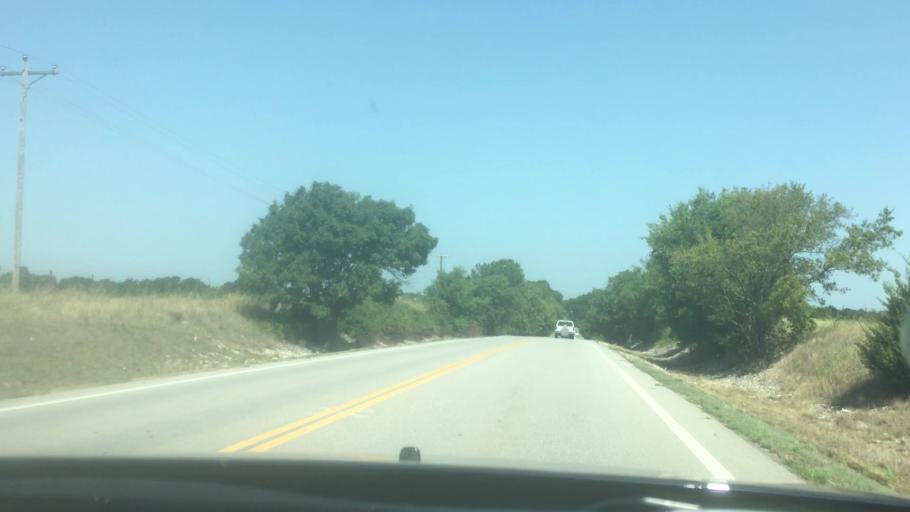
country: US
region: Oklahoma
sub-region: Bryan County
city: Durant
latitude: 34.1660
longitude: -96.4018
